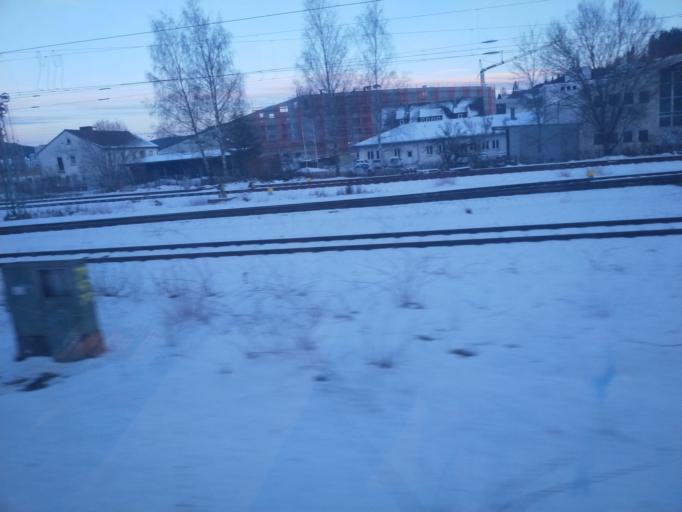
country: DE
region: Baden-Wuerttemberg
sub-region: Freiburg Region
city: Tuttlingen
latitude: 47.9825
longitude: 8.8001
